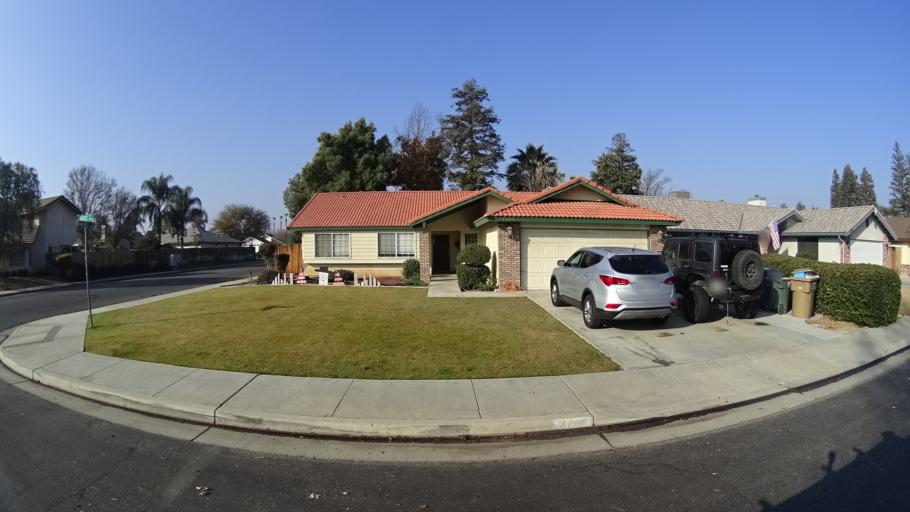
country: US
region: California
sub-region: Kern County
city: Greenacres
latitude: 35.3935
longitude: -119.1083
